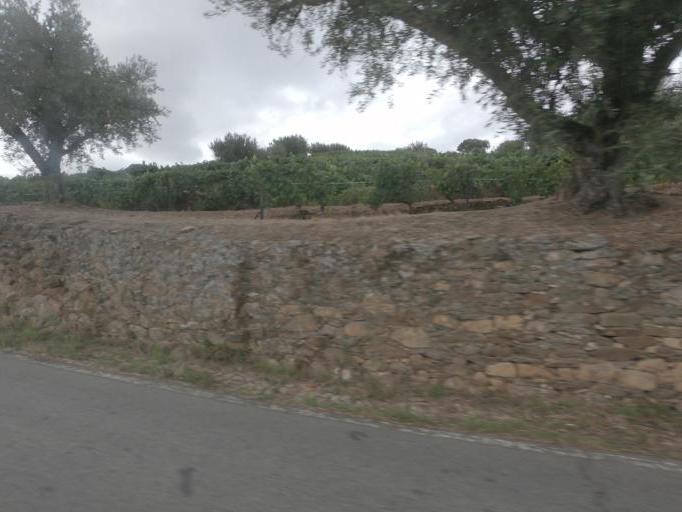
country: PT
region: Vila Real
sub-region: Sabrosa
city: Sabrosa
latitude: 41.2800
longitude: -7.5524
